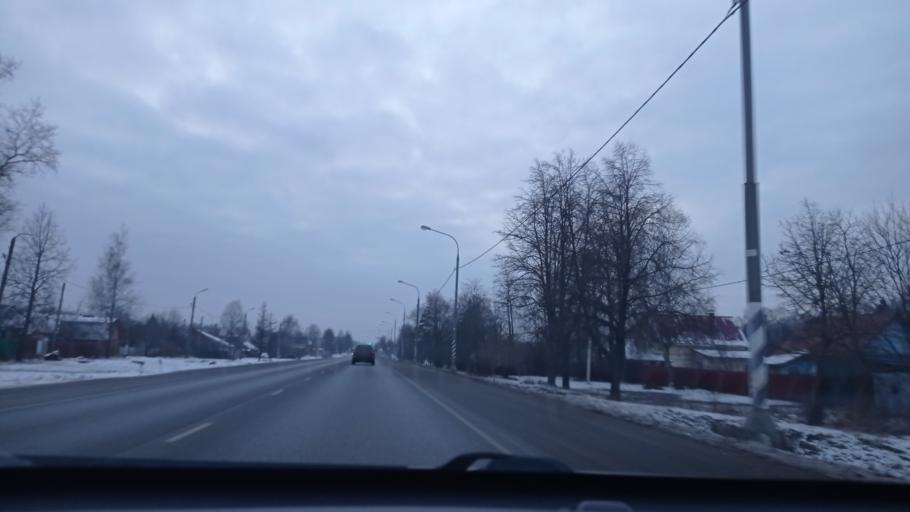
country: RU
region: Kaluga
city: Belousovo
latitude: 55.0982
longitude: 36.6800
